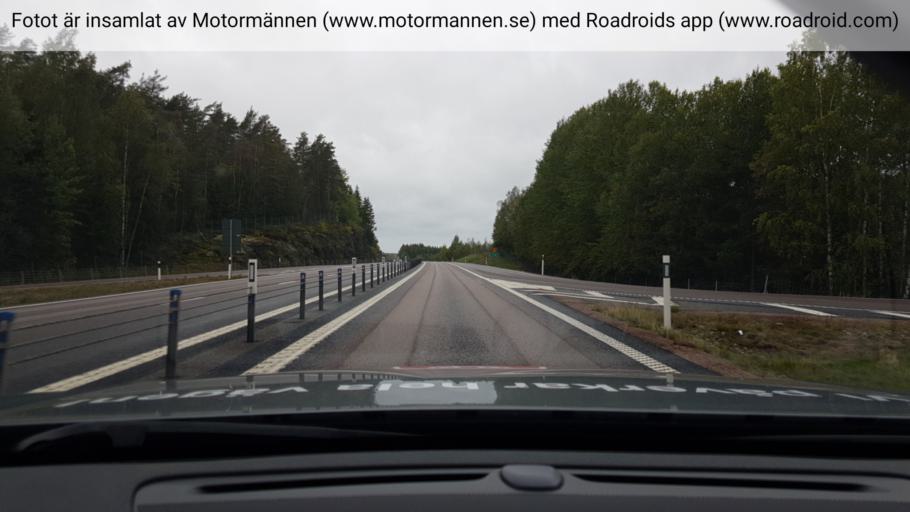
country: SE
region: Vaermland
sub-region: Karlstads Kommun
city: Skattkarr
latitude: 59.3906
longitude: 13.8504
